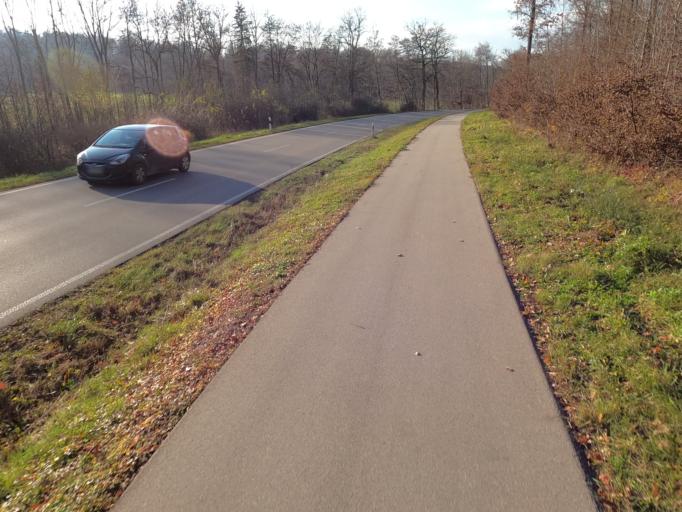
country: DE
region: Baden-Wuerttemberg
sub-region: Regierungsbezirk Stuttgart
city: Schlierbach
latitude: 48.6678
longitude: 9.5340
